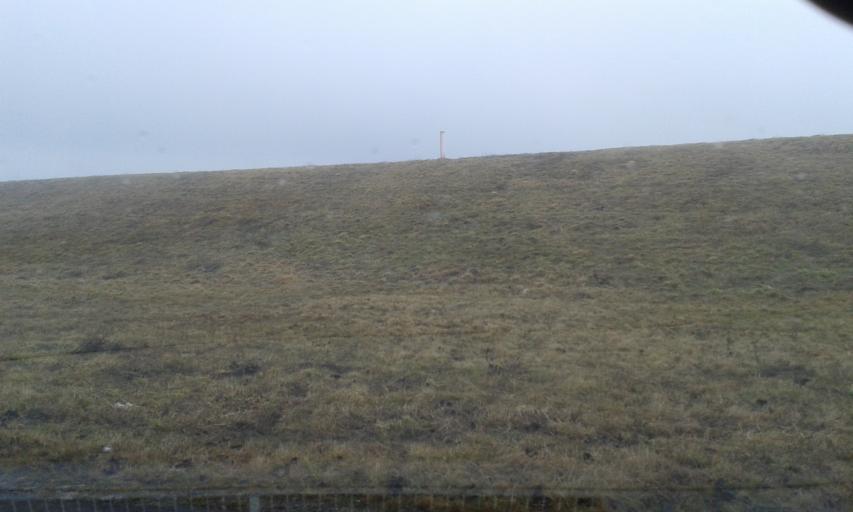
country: SK
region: Nitriansky
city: Tlmace
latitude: 48.2723
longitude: 18.5222
